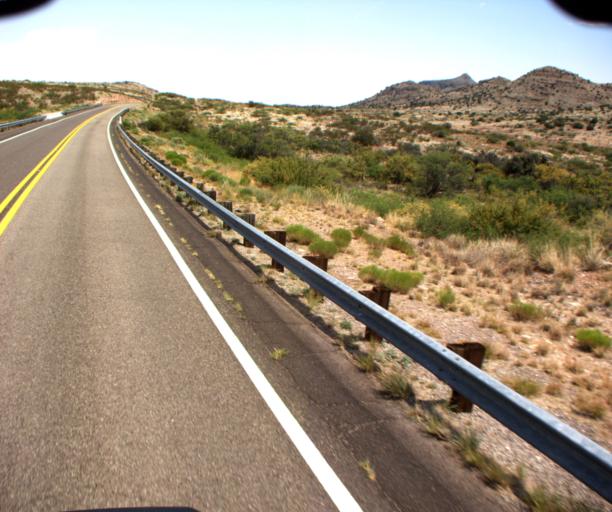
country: US
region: Arizona
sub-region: Greenlee County
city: Clifton
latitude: 32.7782
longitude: -109.2962
